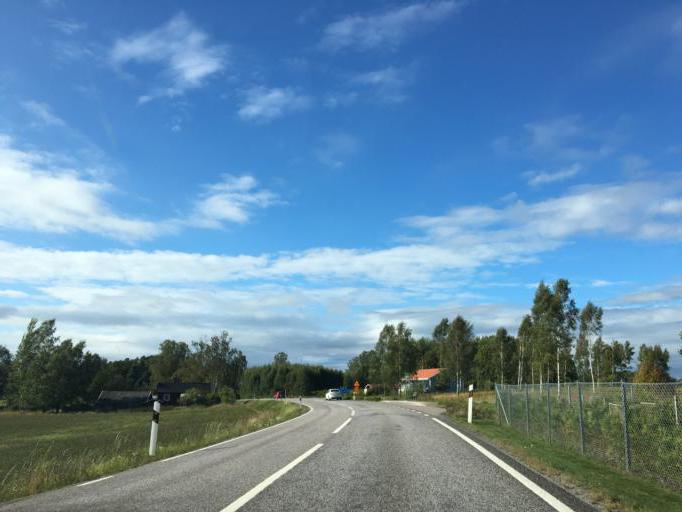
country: SE
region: Soedermanland
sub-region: Nykopings Kommun
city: Stigtomta
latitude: 58.8696
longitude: 16.8991
